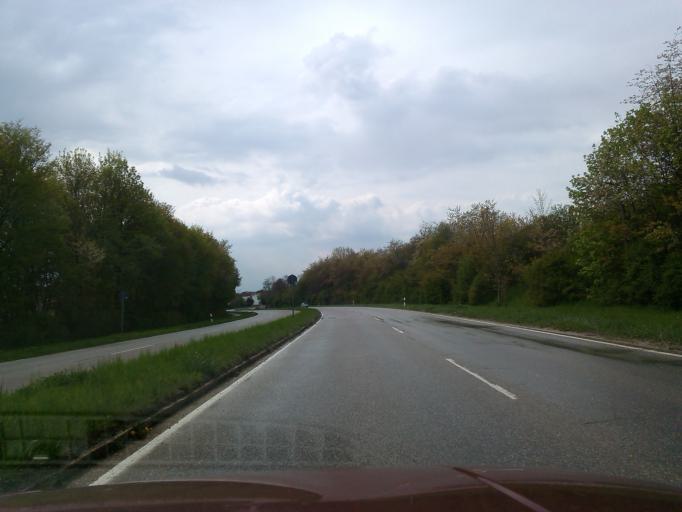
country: DE
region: Bavaria
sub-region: Upper Bavaria
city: Grafelfing
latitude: 48.1153
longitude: 11.4461
